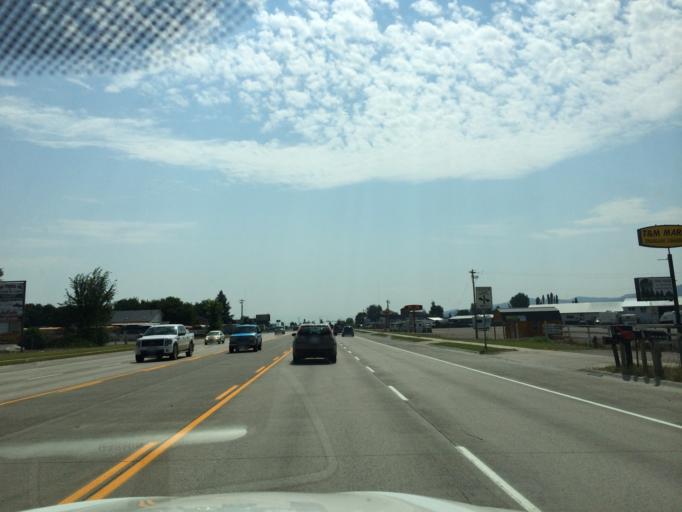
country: US
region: Montana
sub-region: Flathead County
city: Kalispell
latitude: 48.1706
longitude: -114.2938
